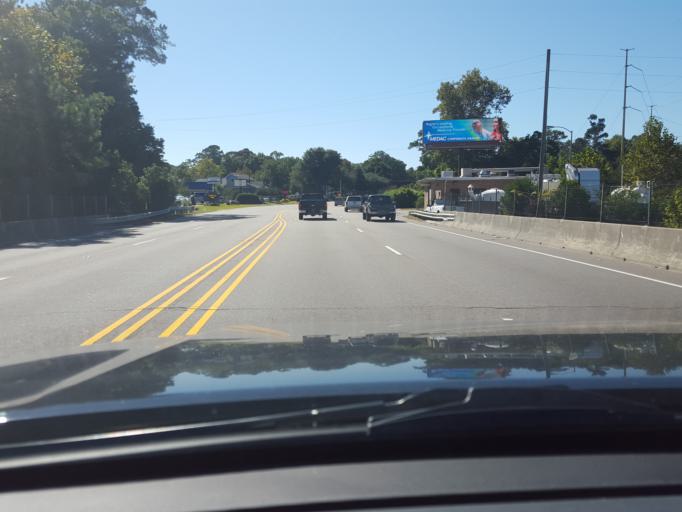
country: US
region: North Carolina
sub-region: New Hanover County
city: Seagate
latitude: 34.2147
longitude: -77.8343
